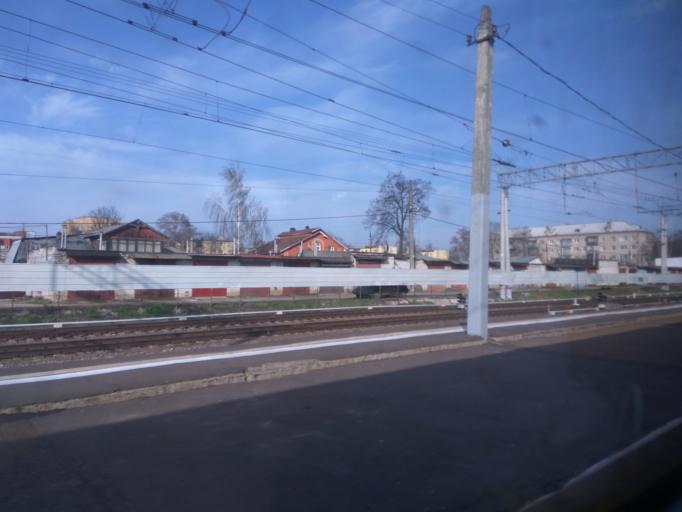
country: RU
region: Moskovskaya
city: Ramenskoye
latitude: 55.5612
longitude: 38.2376
